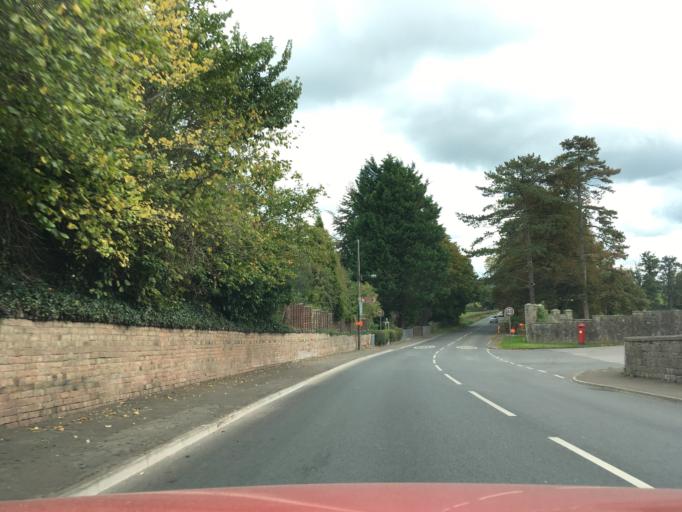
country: GB
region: England
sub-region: Gloucestershire
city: Berkeley
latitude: 51.6911
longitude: -2.4549
